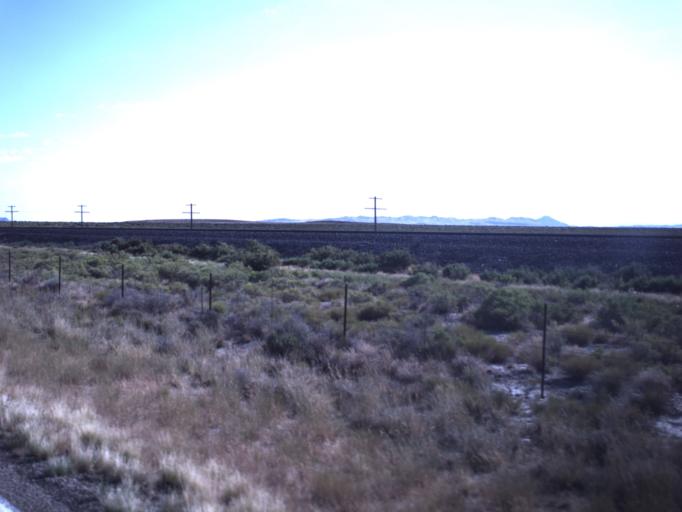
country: US
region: Utah
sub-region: Beaver County
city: Milford
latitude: 38.6217
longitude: -112.9850
